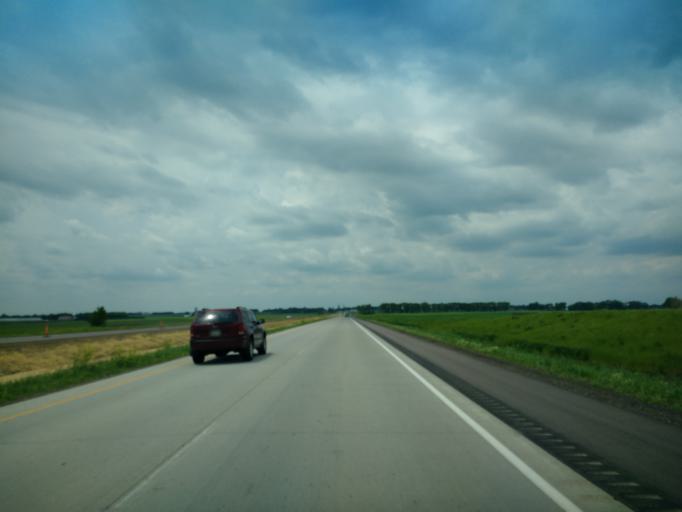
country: US
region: Minnesota
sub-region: Cottonwood County
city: Mountain Lake
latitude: 43.9178
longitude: -95.0034
